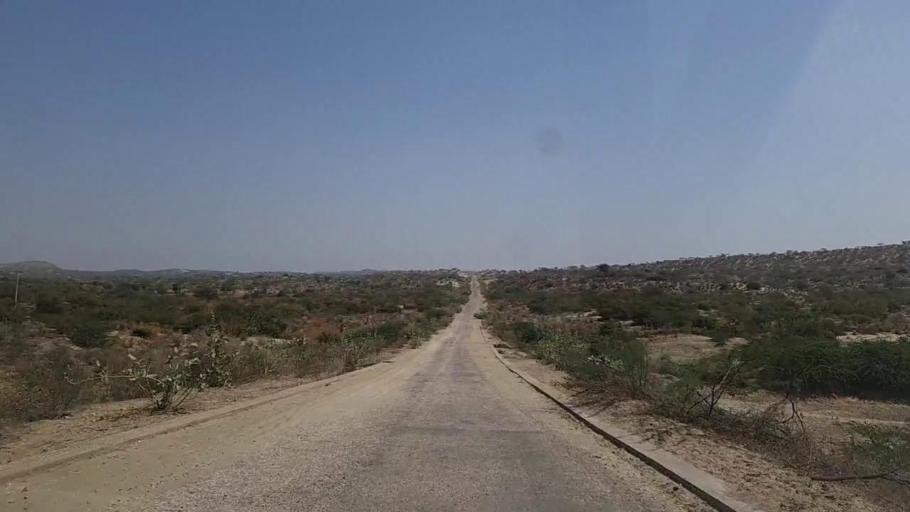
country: PK
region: Sindh
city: Diplo
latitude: 24.5137
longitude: 69.3954
